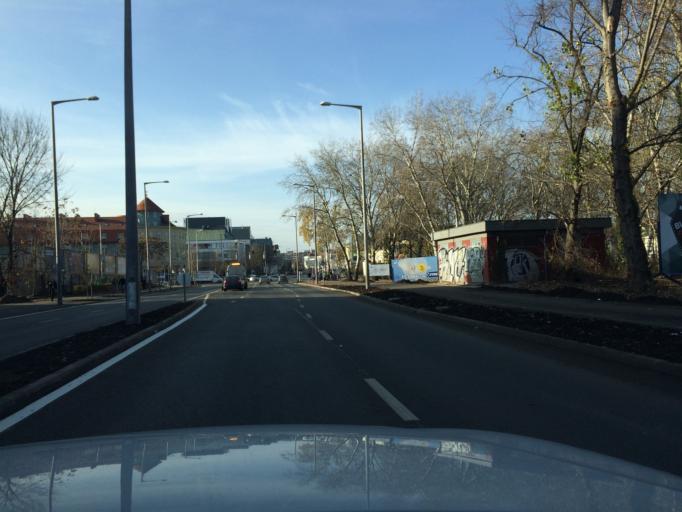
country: HU
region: Szabolcs-Szatmar-Bereg
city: Nyiregyhaza
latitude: 47.9574
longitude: 21.7230
